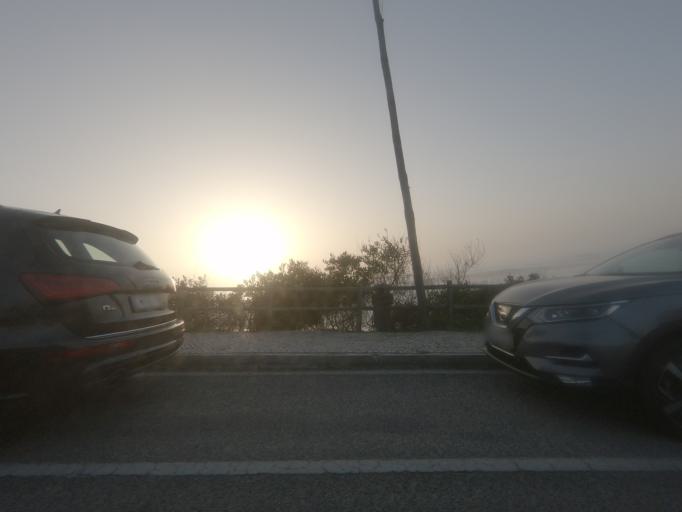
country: PT
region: Leiria
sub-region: Alcobaca
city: Pataias
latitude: 39.7548
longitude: -9.0323
